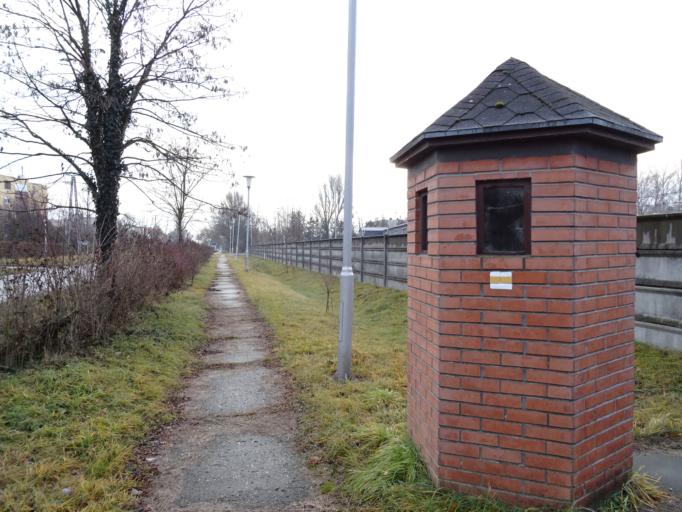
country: HU
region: Bacs-Kiskun
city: Szabadszallas
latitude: 46.8885
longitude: 19.2197
